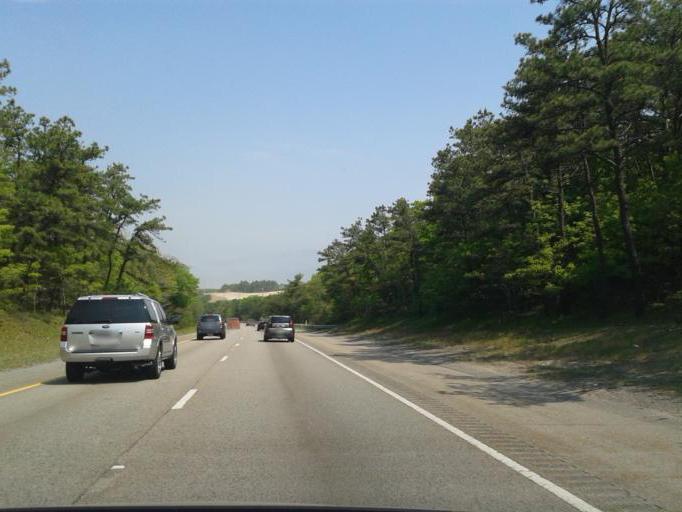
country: US
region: Massachusetts
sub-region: Barnstable County
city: Sagamore
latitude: 41.8245
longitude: -70.5586
